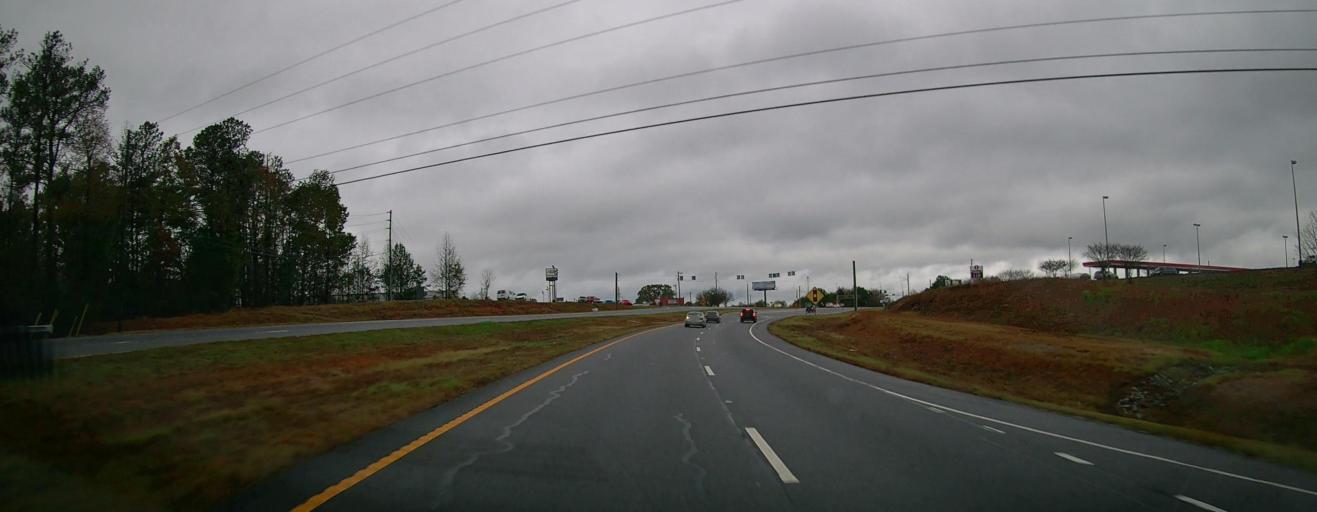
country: US
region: Georgia
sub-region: Jackson County
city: Commerce
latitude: 34.1804
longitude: -83.4424
